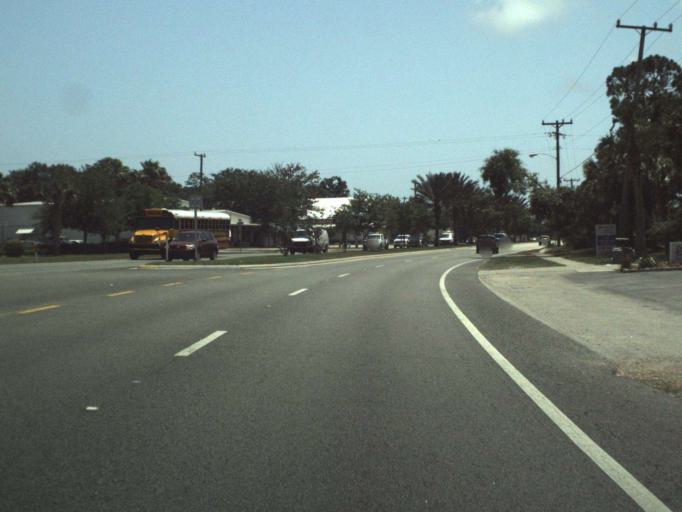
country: US
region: Florida
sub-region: Volusia County
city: Ormond Beach
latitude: 29.2883
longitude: -81.0654
